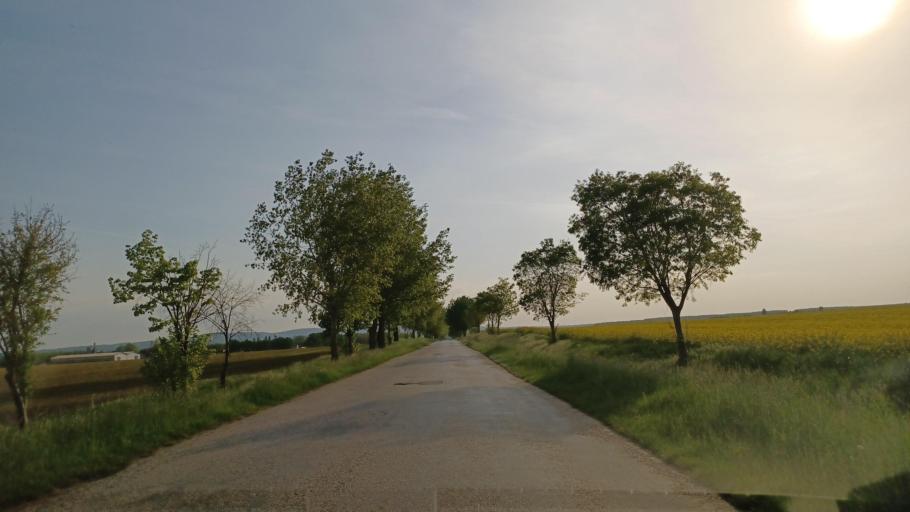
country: HU
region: Baranya
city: Kozarmisleny
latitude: 45.9508
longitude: 18.3734
